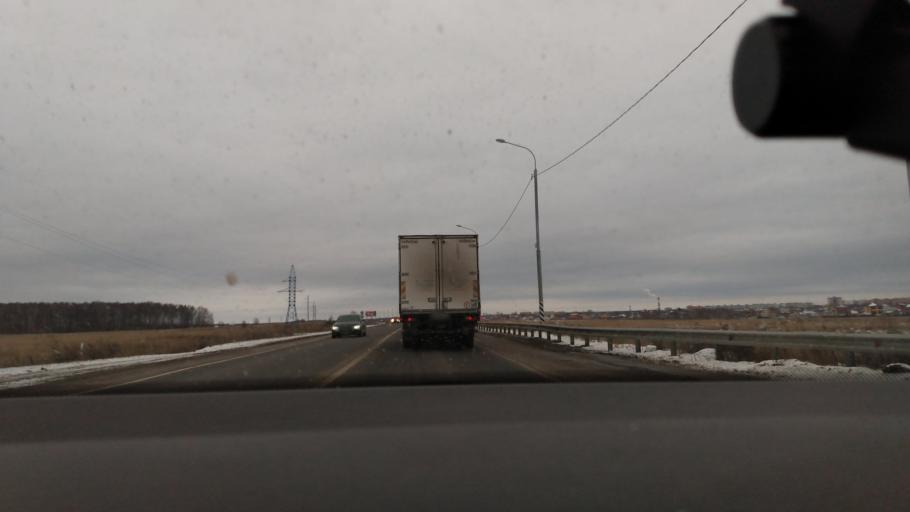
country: RU
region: Moskovskaya
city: Yegor'yevsk
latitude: 55.4026
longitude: 39.0582
